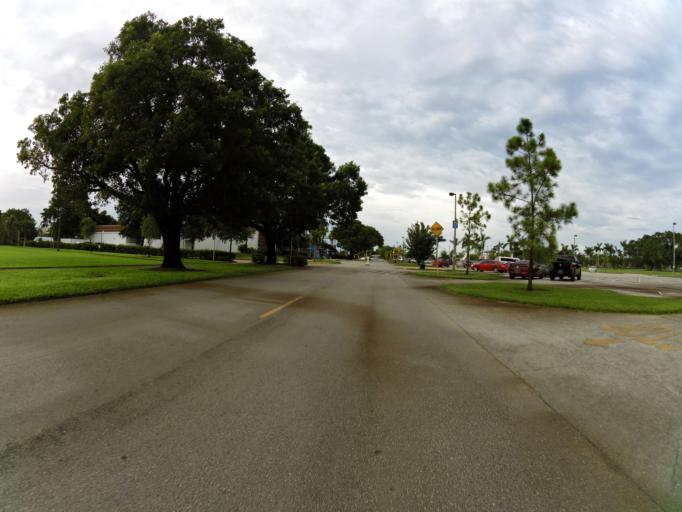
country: US
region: Florida
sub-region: Broward County
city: Davie
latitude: 26.0780
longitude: -80.2338
